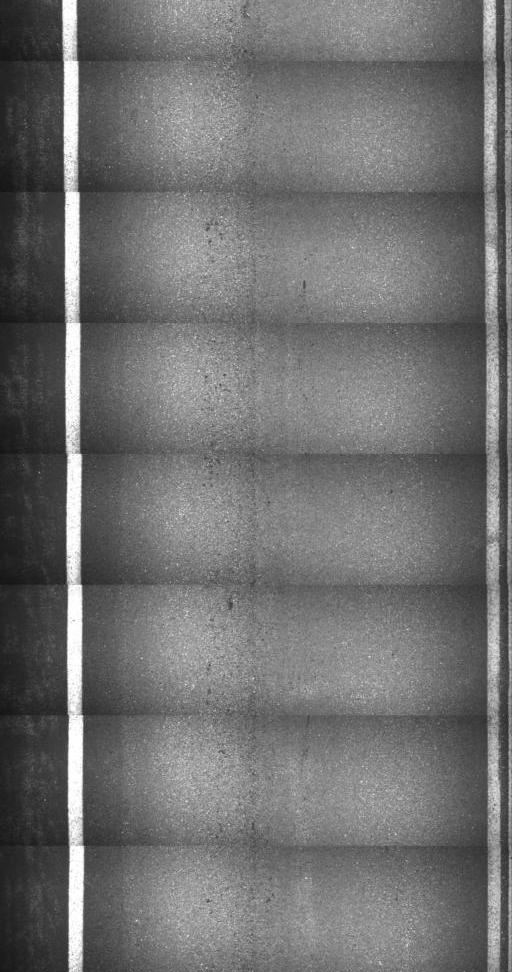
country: US
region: Vermont
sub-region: Caledonia County
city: Lyndonville
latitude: 44.7393
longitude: -71.8821
